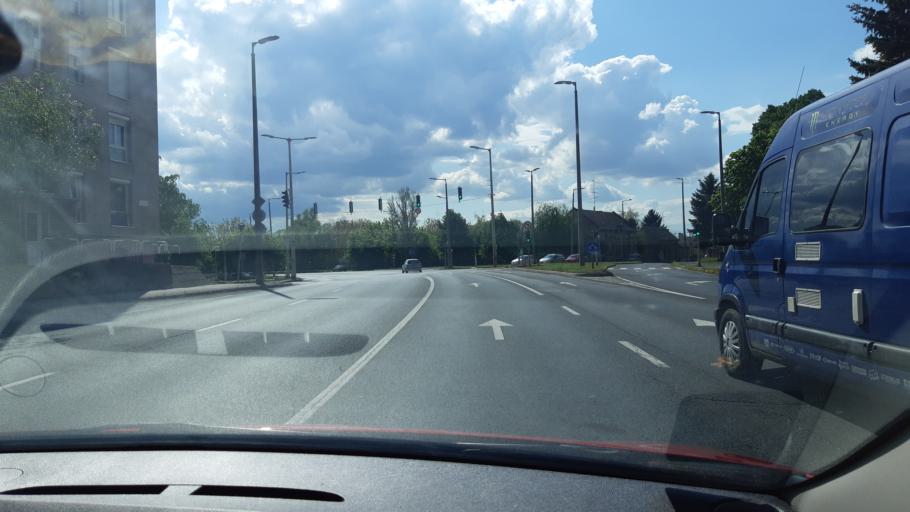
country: HU
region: Somogy
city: Kaposvar
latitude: 46.3635
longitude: 17.7792
